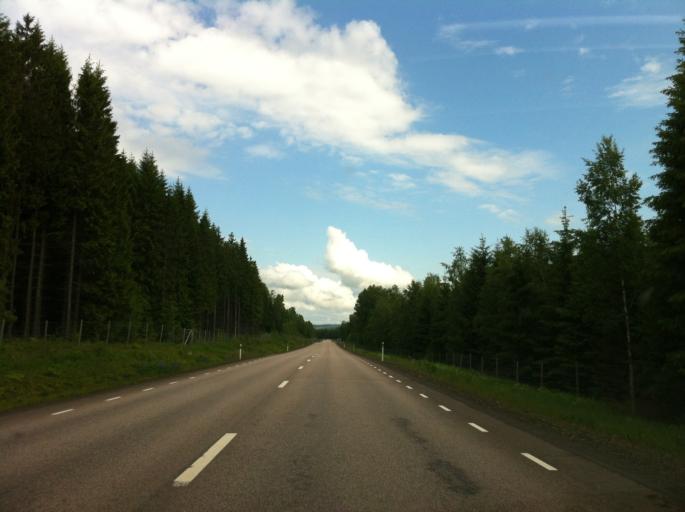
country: SE
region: Vaermland
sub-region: Sunne Kommun
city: Sunne
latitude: 59.7557
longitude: 13.1168
